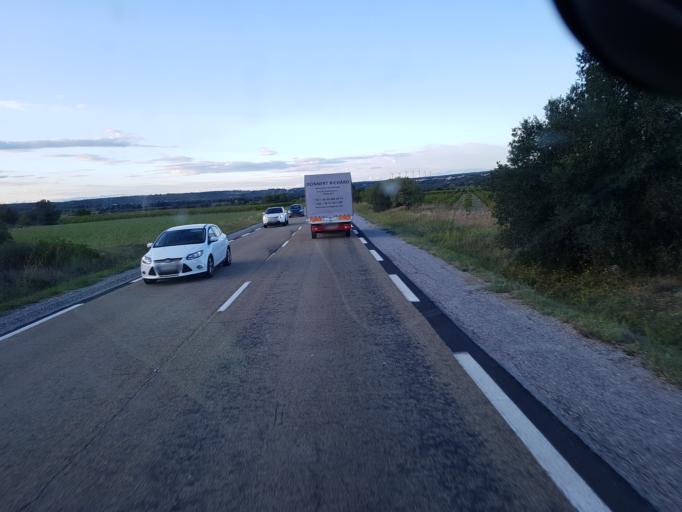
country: FR
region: Languedoc-Roussillon
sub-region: Departement de l'Aude
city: Leucate
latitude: 42.9503
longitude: 2.9871
